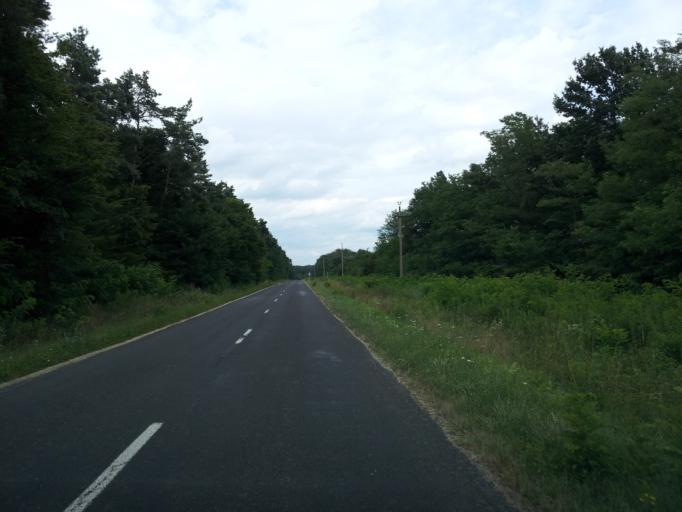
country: HU
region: Zala
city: Turje
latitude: 47.0476
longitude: 17.0006
